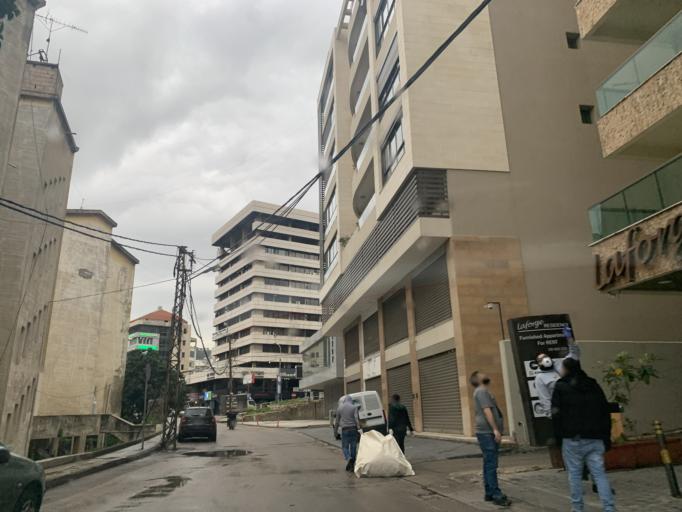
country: LB
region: Mont-Liban
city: Djounie
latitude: 33.9815
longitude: 35.6259
